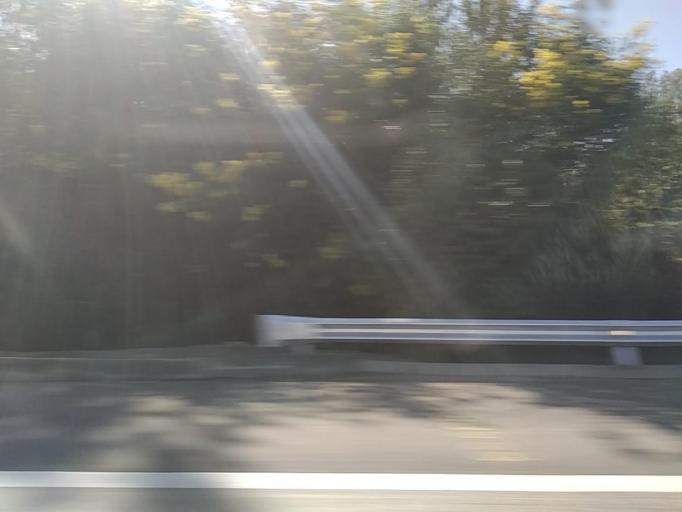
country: CL
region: Valparaiso
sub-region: Provincia de Marga Marga
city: Quilpue
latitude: -33.2403
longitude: -71.4539
